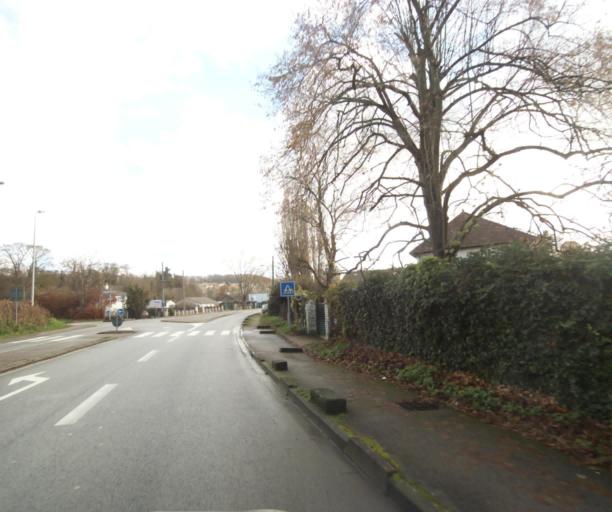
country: FR
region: Ile-de-France
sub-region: Departement des Yvelines
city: Hardricourt
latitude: 49.0141
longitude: 1.8999
